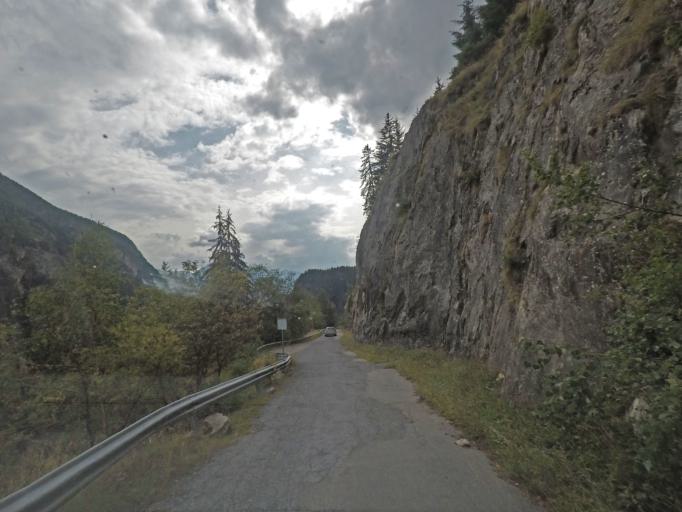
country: CH
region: Valais
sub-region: Brig District
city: Naters
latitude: 46.3688
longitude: 7.9996
